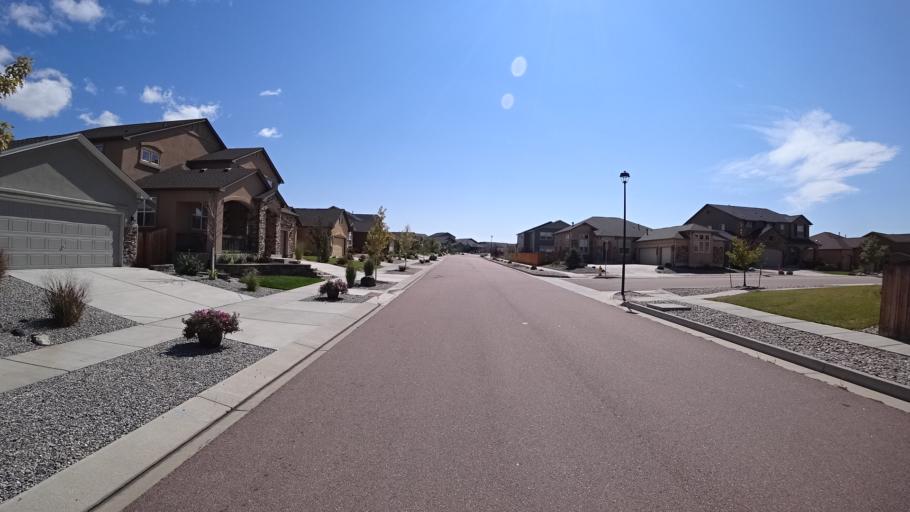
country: US
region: Colorado
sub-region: El Paso County
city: Cimarron Hills
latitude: 38.9317
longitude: -104.6860
